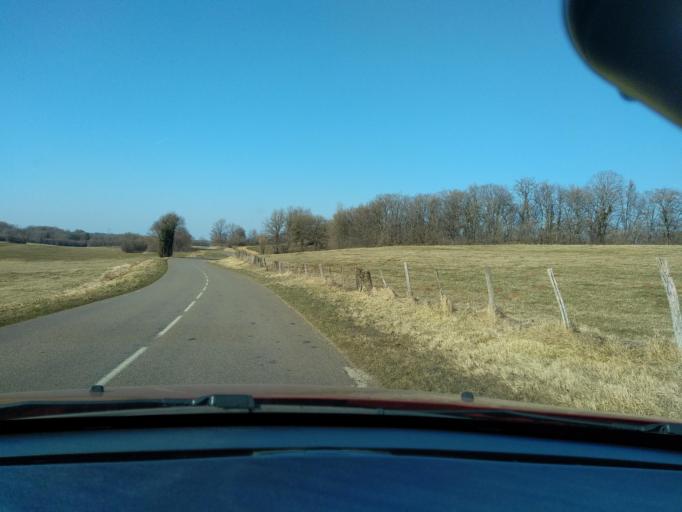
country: FR
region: Franche-Comte
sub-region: Departement du Jura
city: Perrigny
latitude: 46.6200
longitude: 5.6414
